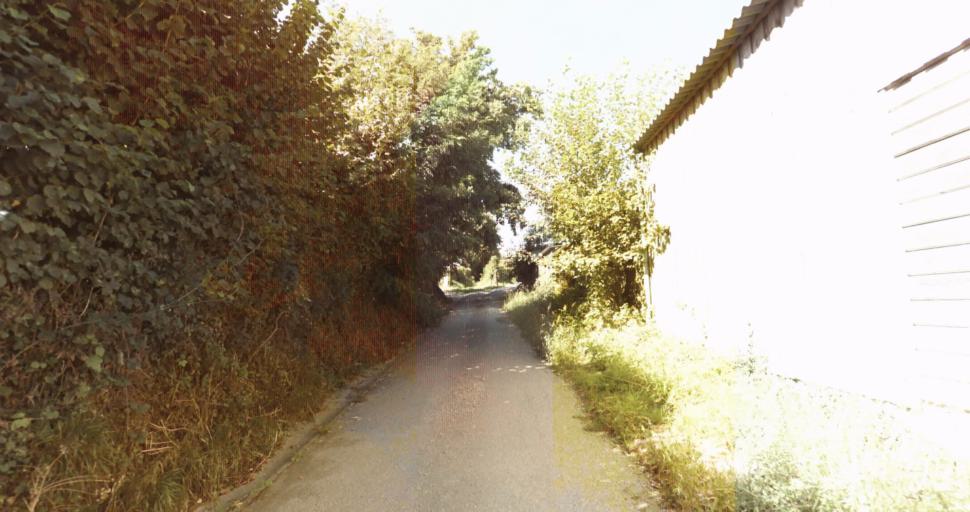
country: FR
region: Lower Normandy
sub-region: Departement de l'Orne
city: Gace
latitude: 48.7693
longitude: 0.2604
